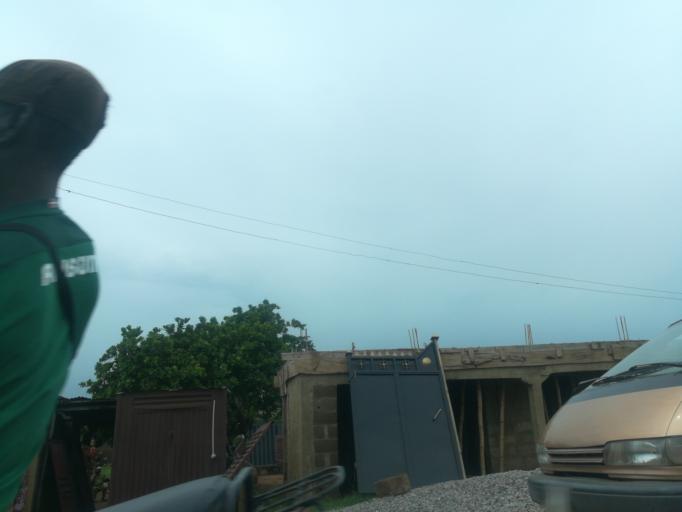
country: NG
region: Oyo
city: Ibadan
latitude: 7.3303
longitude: 3.8924
